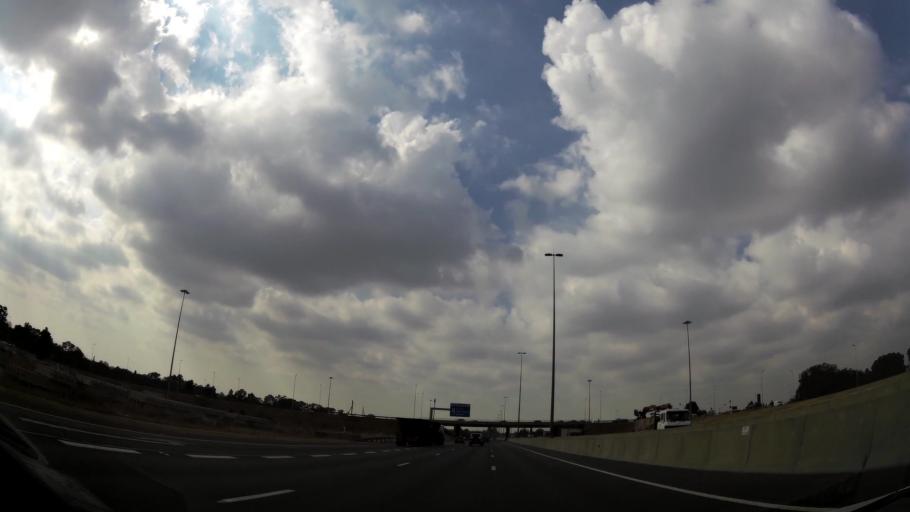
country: ZA
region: Gauteng
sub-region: Ekurhuleni Metropolitan Municipality
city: Boksburg
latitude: -26.1737
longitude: 28.2786
